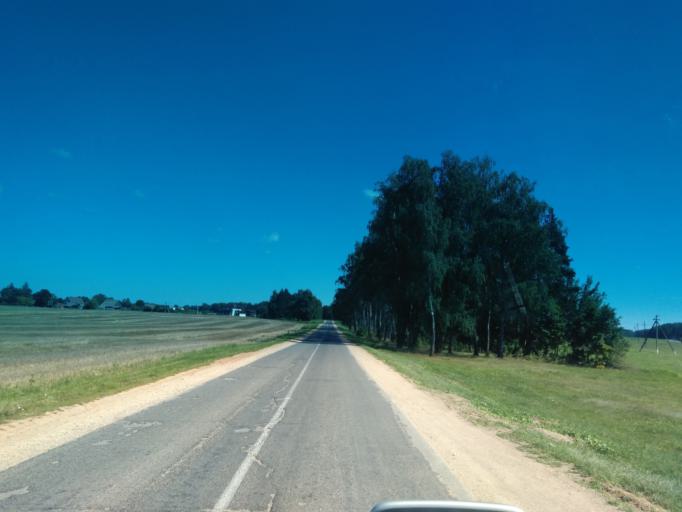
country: BY
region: Minsk
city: Stan'kava
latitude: 53.6271
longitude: 27.2589
